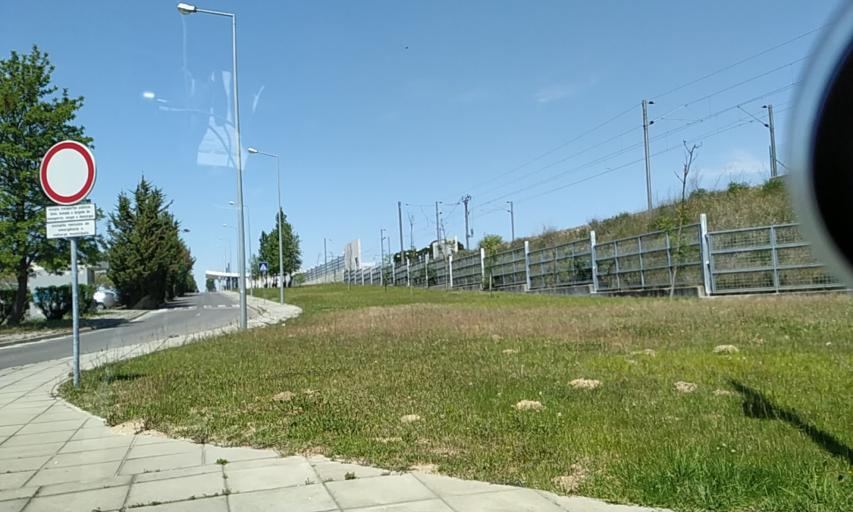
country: PT
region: Setubal
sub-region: Palmela
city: Palmela
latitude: 38.5693
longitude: -8.8727
